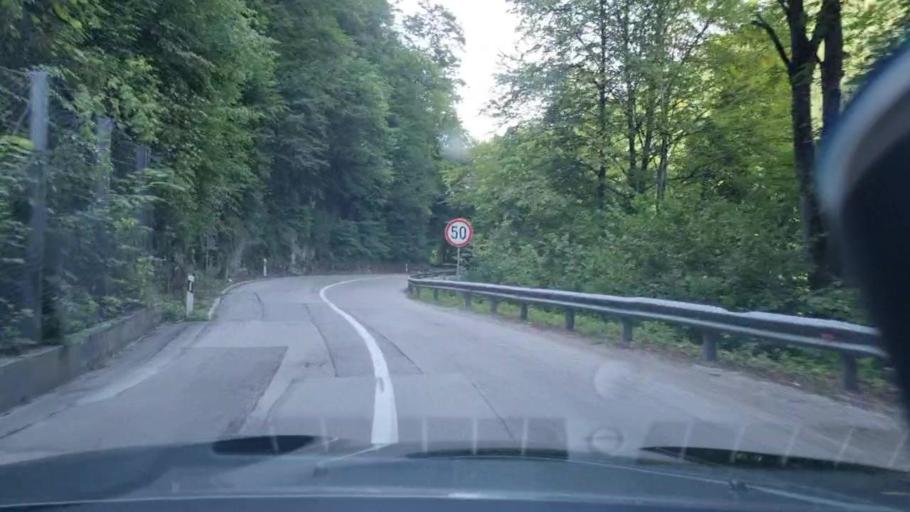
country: BA
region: Federation of Bosnia and Herzegovina
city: Stijena
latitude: 44.8889
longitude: 16.0543
